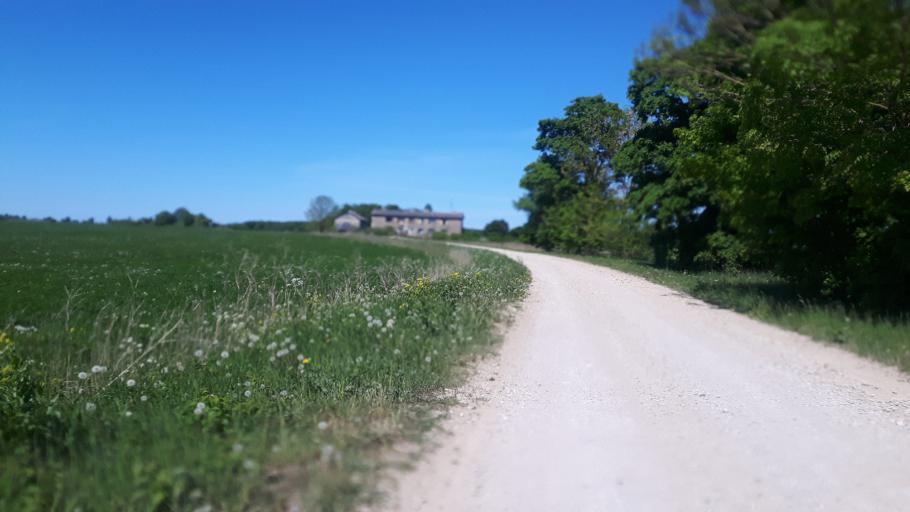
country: EE
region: Ida-Virumaa
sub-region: Toila vald
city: Voka
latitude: 59.4011
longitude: 27.6661
